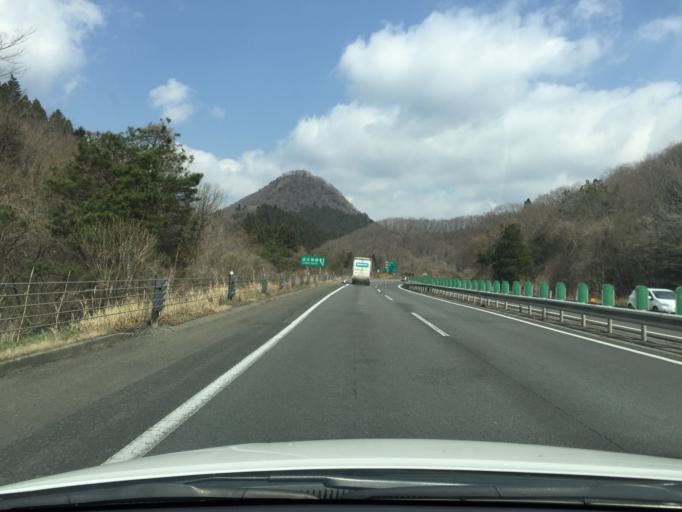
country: JP
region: Miyagi
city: Sendai
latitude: 38.2248
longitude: 140.8032
